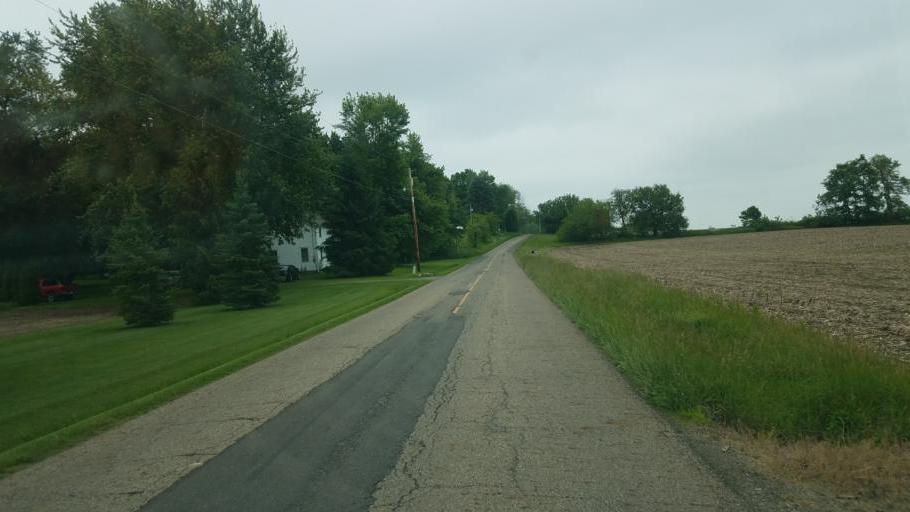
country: US
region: Ohio
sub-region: Knox County
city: Centerburg
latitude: 40.3303
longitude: -82.7270
